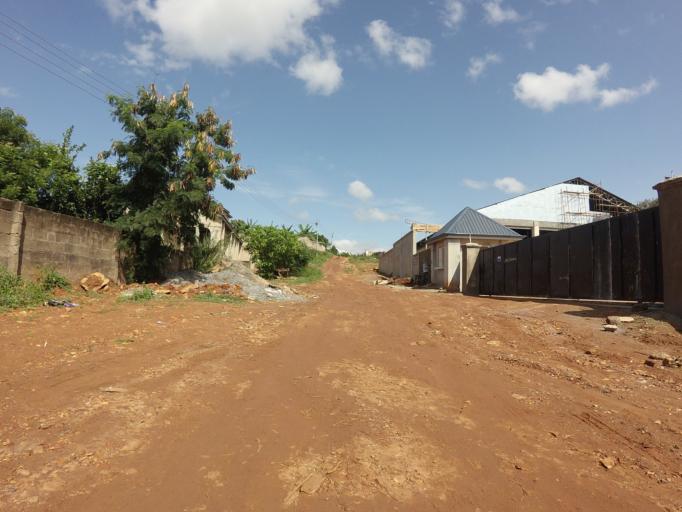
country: GH
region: Eastern
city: Aburi
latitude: 5.8612
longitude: -0.1110
